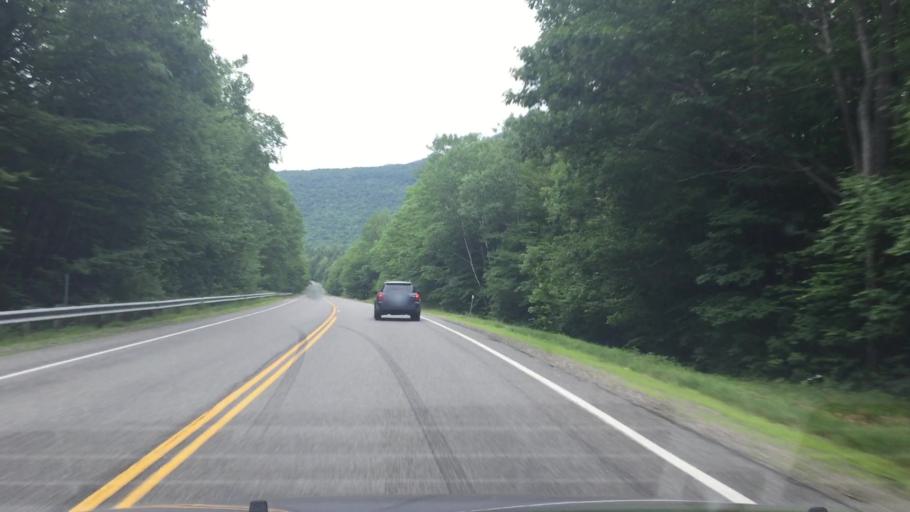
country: US
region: New Hampshire
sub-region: Carroll County
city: North Conway
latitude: 44.0957
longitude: -71.3549
